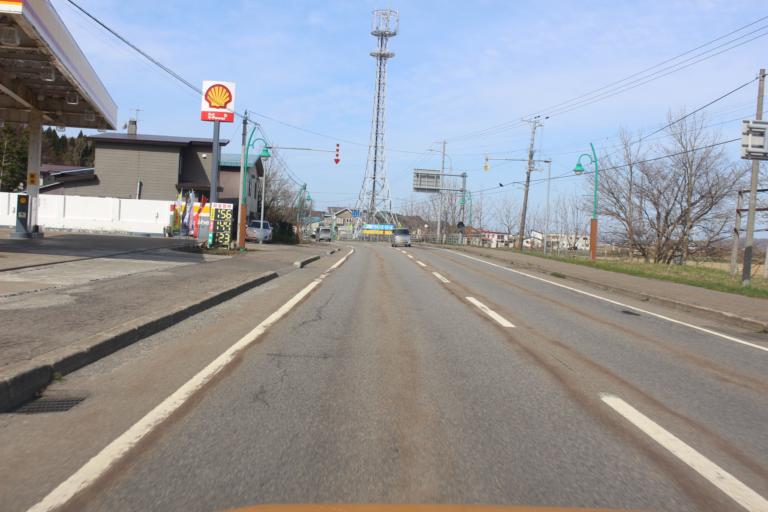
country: JP
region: Hokkaido
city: Kamiiso
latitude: 41.9173
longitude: 140.2204
